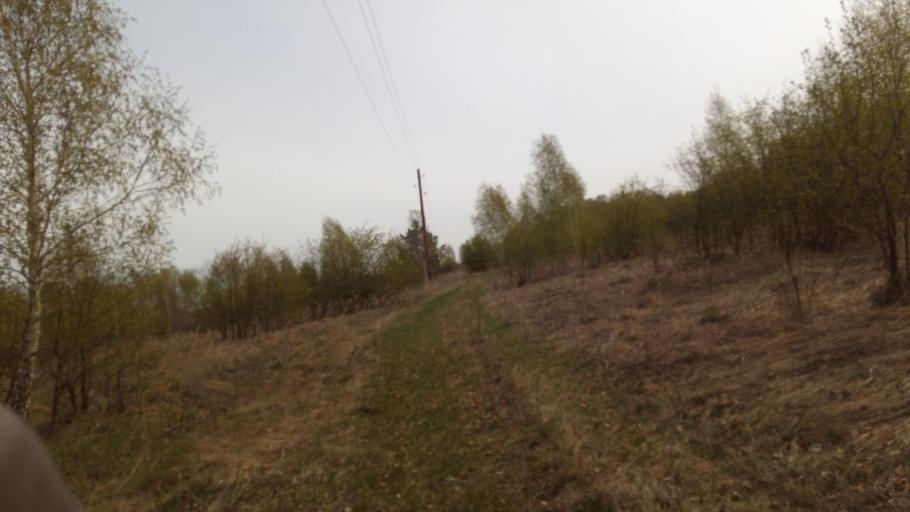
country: RU
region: Chelyabinsk
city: Timiryazevskiy
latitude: 54.9961
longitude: 60.8509
